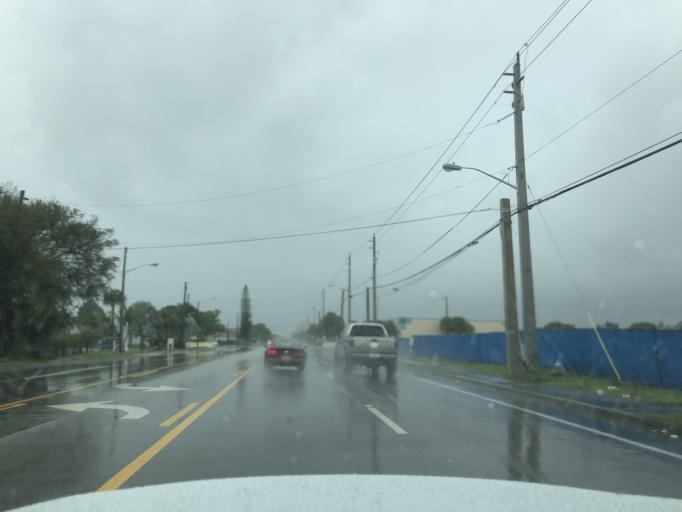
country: US
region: Florida
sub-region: Palm Beach County
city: Royal Palm Estates
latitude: 26.6823
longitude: -80.1201
